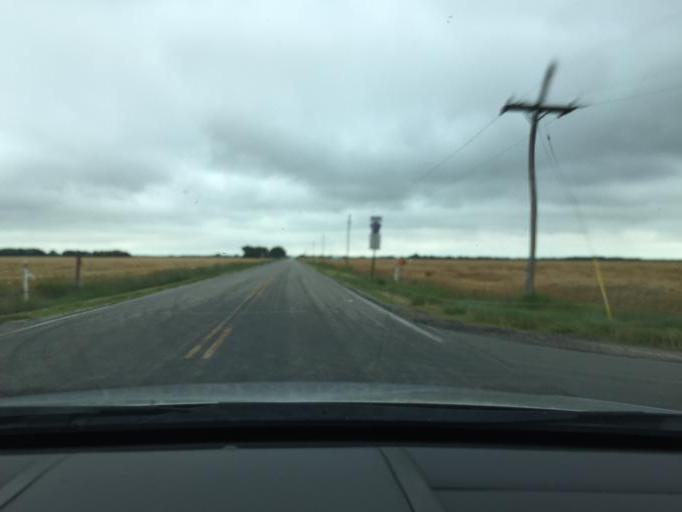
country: US
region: Kansas
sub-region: McPherson County
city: Moundridge
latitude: 38.2031
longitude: -97.5923
